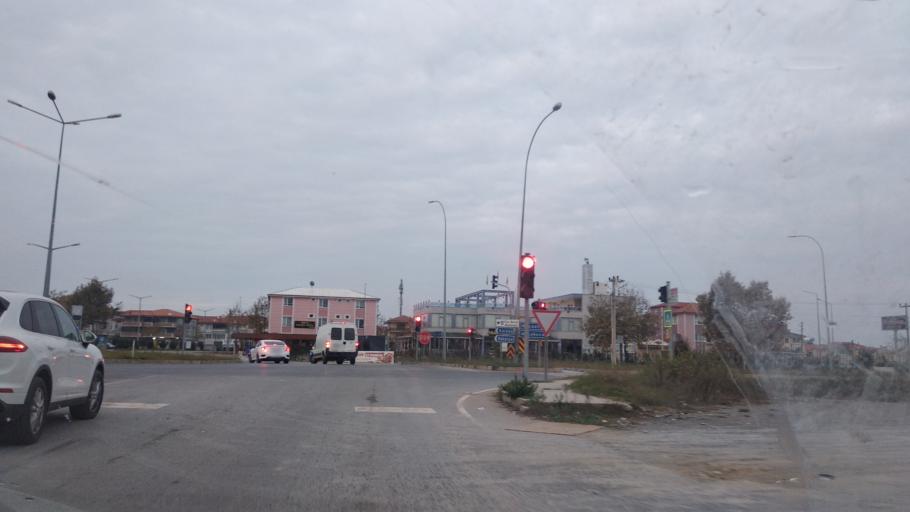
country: TR
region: Sakarya
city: Karasu
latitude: 41.0871
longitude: 30.7406
